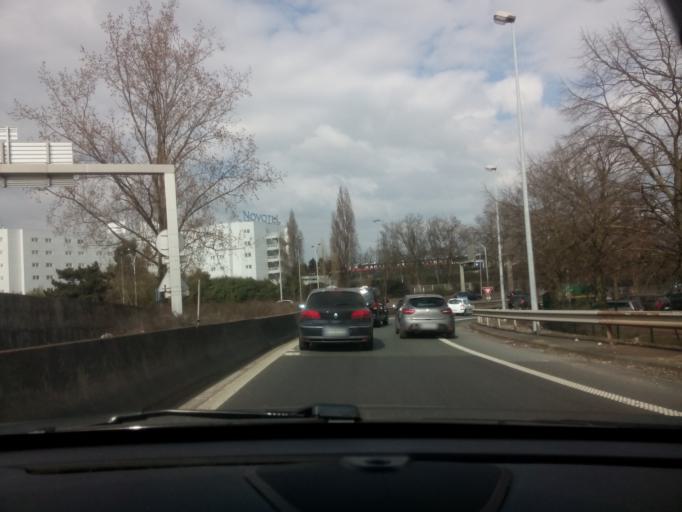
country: FR
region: Ile-de-France
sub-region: Departement du Val-de-Marne
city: Rungis
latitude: 48.7535
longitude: 2.3501
